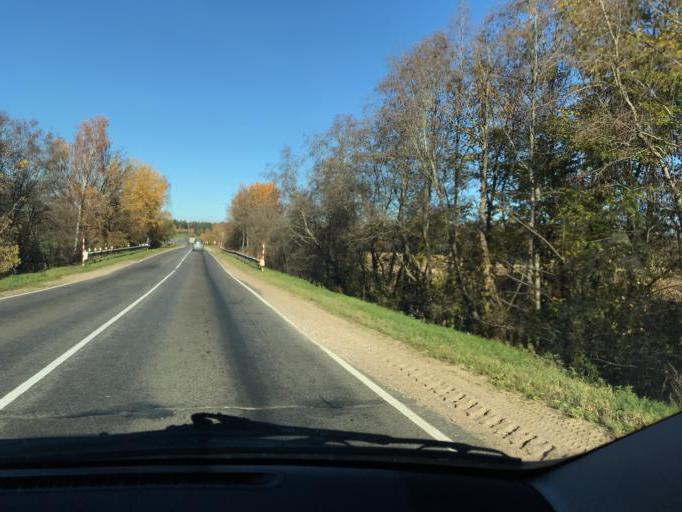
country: BY
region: Vitebsk
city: Polatsk
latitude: 55.3081
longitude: 28.7789
